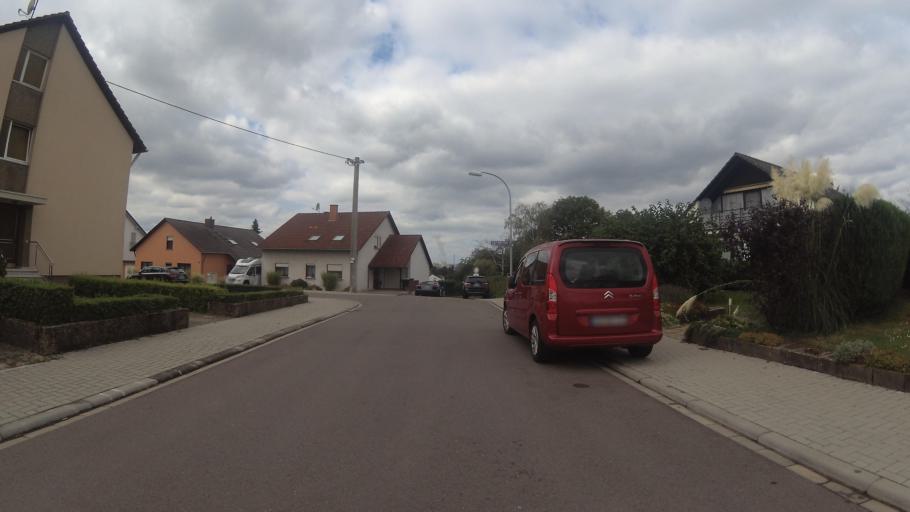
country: FR
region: Lorraine
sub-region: Departement de la Moselle
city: Schoeneck
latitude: 49.2368
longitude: 6.9208
